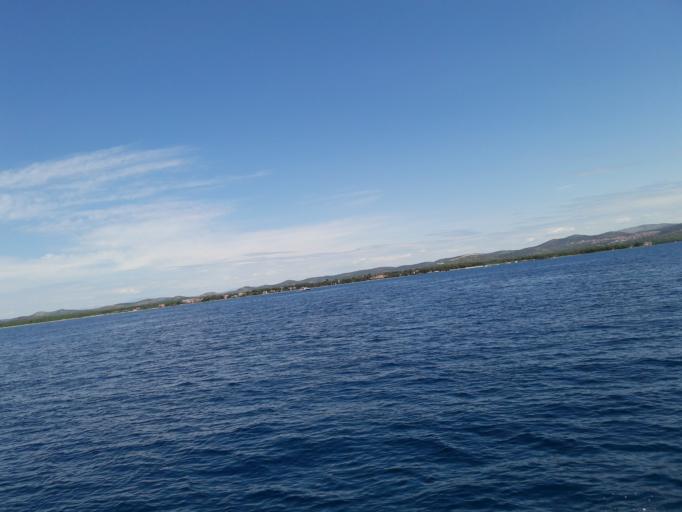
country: HR
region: Sibensko-Kniniska
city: Vodice
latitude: 43.7123
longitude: 15.8355
